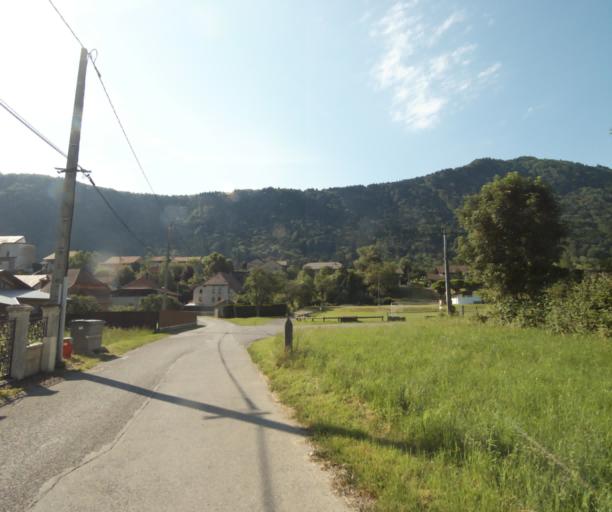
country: FR
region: Rhone-Alpes
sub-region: Departement de la Haute-Savoie
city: Allinges
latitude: 46.3132
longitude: 6.4878
